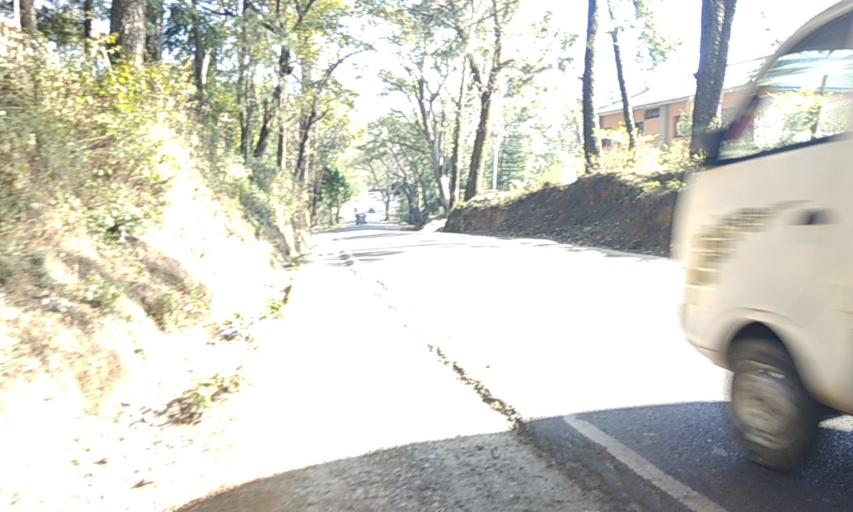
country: IN
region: Himachal Pradesh
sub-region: Kangra
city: Palampur
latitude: 32.1045
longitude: 76.5536
